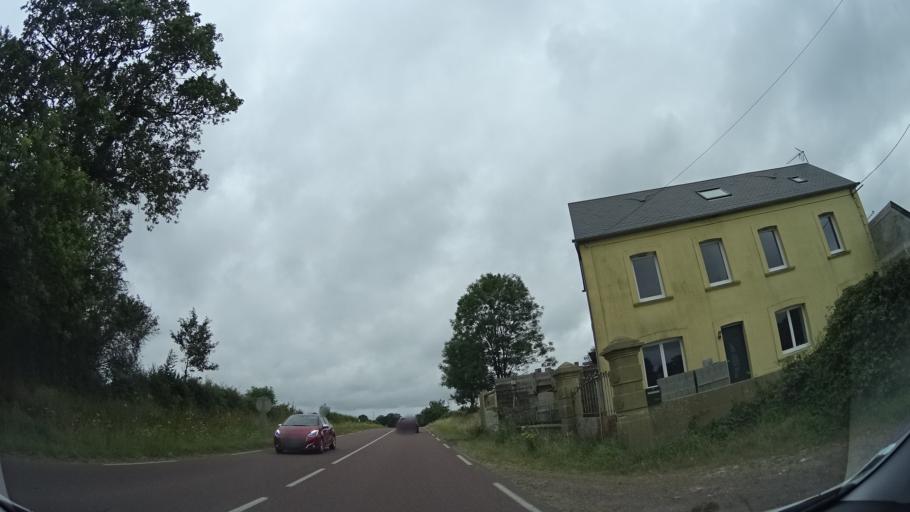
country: FR
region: Lower Normandy
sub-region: Departement de la Manche
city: La Haye-du-Puits
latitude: 49.2725
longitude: -1.5400
